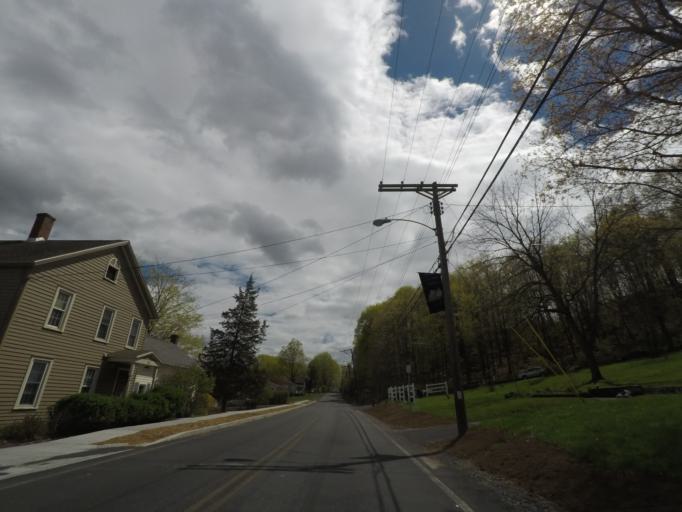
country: US
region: New York
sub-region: Albany County
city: Ravena
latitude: 42.4702
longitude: -73.7923
